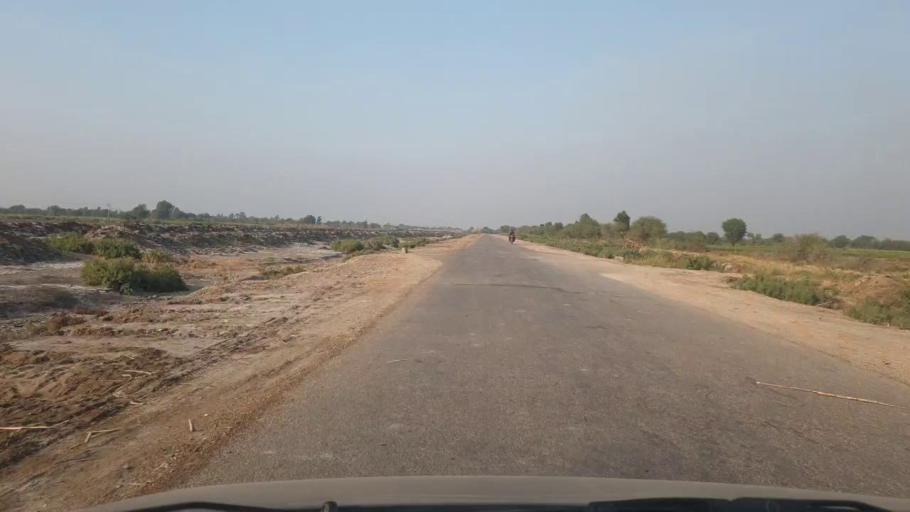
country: PK
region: Sindh
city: Mirwah Gorchani
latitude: 25.3603
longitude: 69.1755
